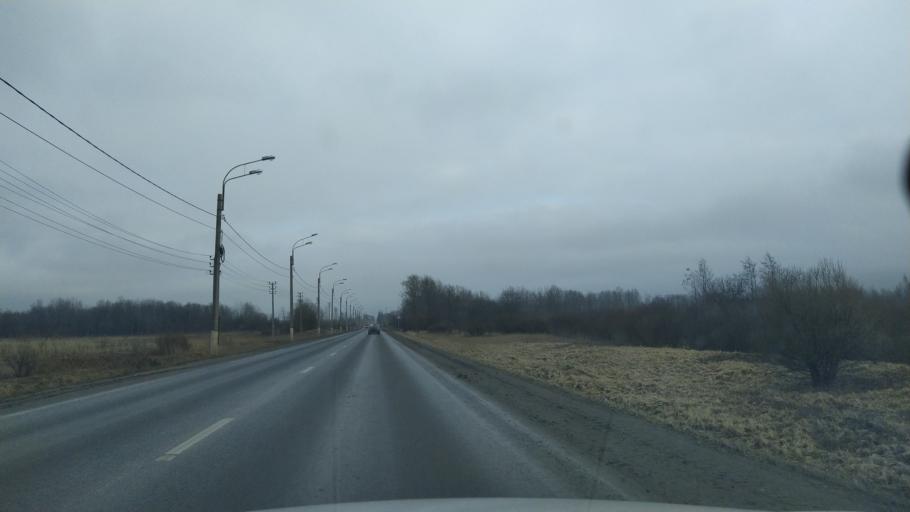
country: RU
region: St.-Petersburg
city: Aleksandrovskaya
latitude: 59.7135
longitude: 30.3043
